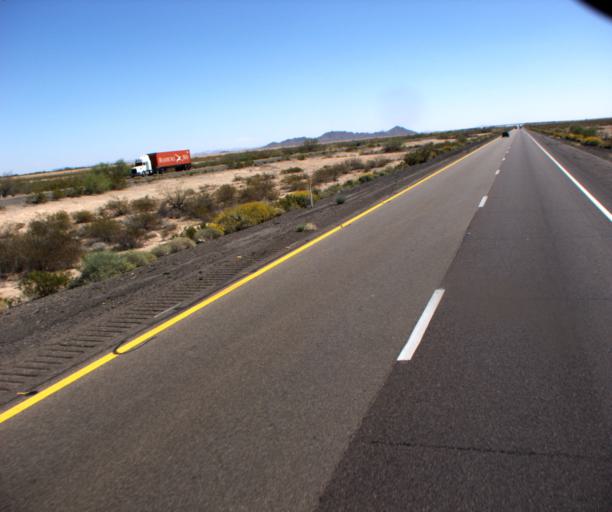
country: US
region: Arizona
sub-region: La Paz County
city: Salome
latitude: 33.5986
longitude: -113.5518
